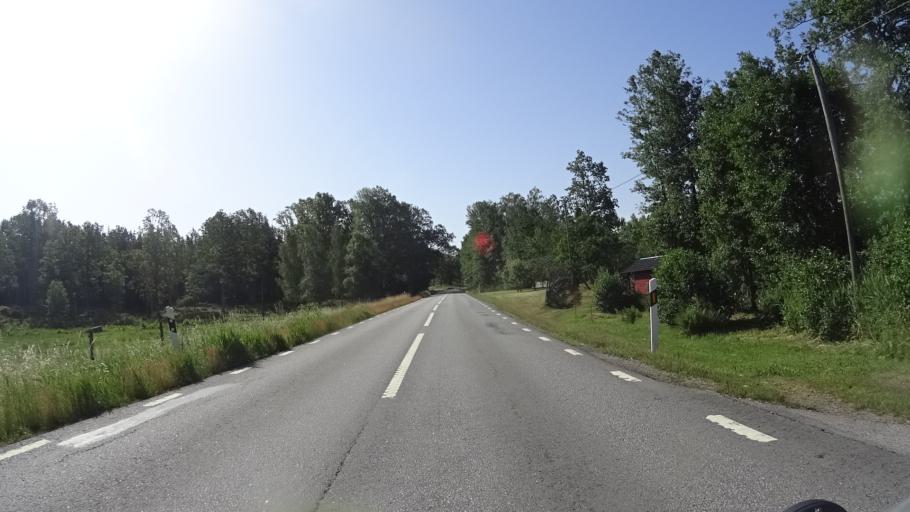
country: SE
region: OEstergoetland
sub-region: Atvidabergs Kommun
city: Atvidaberg
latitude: 58.0964
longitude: 16.1242
